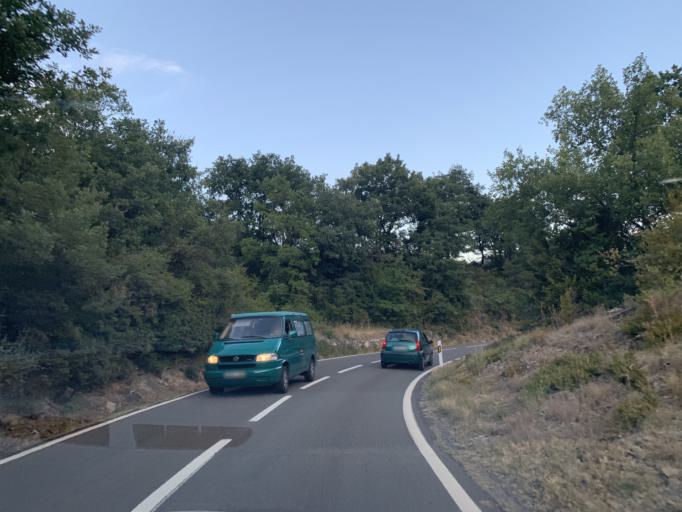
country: ES
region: Aragon
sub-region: Provincia de Huesca
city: Fiscal
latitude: 42.5110
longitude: -0.1260
